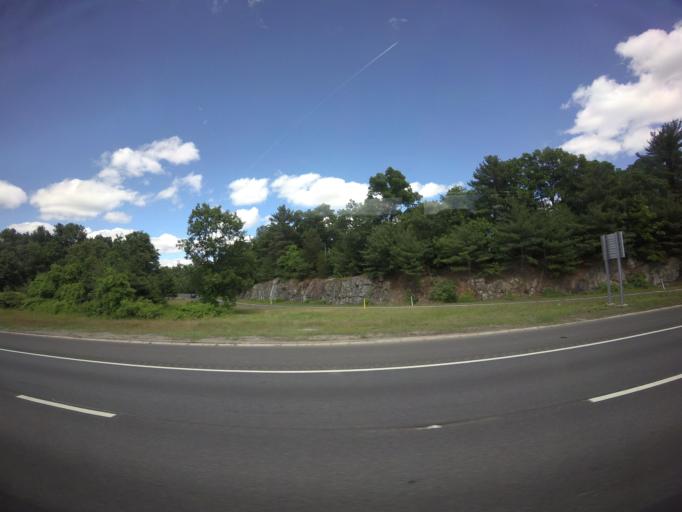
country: US
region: Massachusetts
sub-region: Middlesex County
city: Wilmington
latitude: 42.5753
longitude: -71.1507
